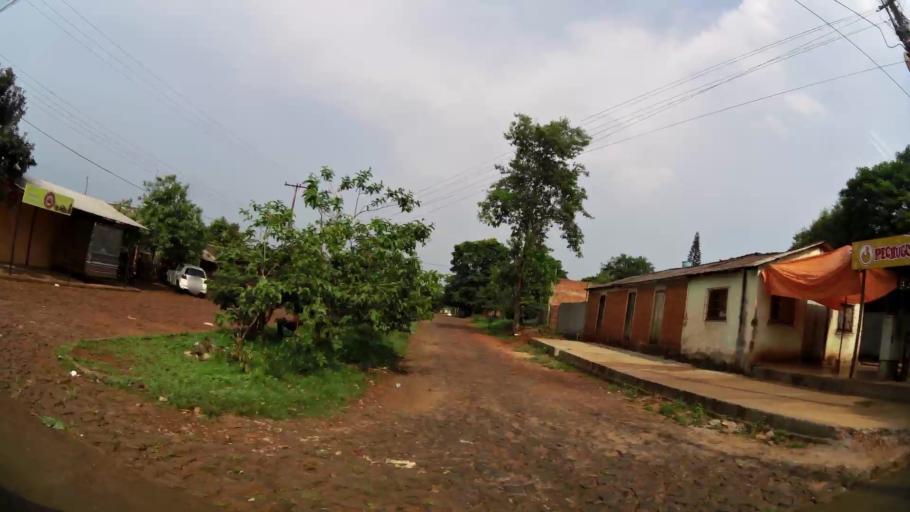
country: PY
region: Alto Parana
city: Ciudad del Este
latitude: -25.4952
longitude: -54.6498
